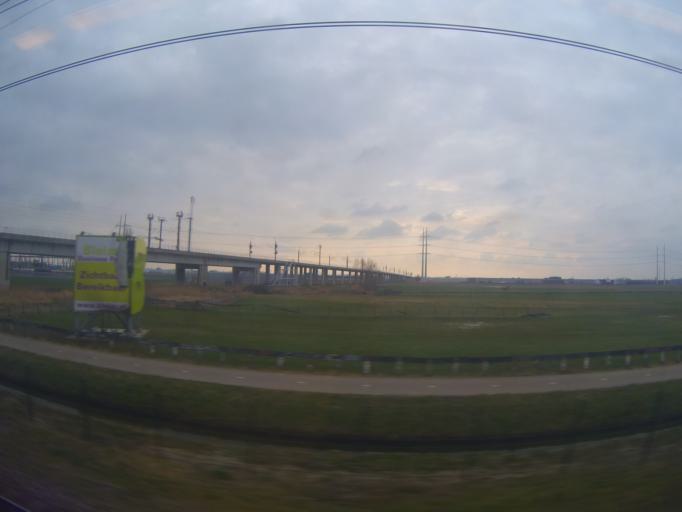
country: NL
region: South Holland
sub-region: Gemeente Lansingerland
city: Bleiswijk
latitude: 52.0388
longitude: 4.5274
